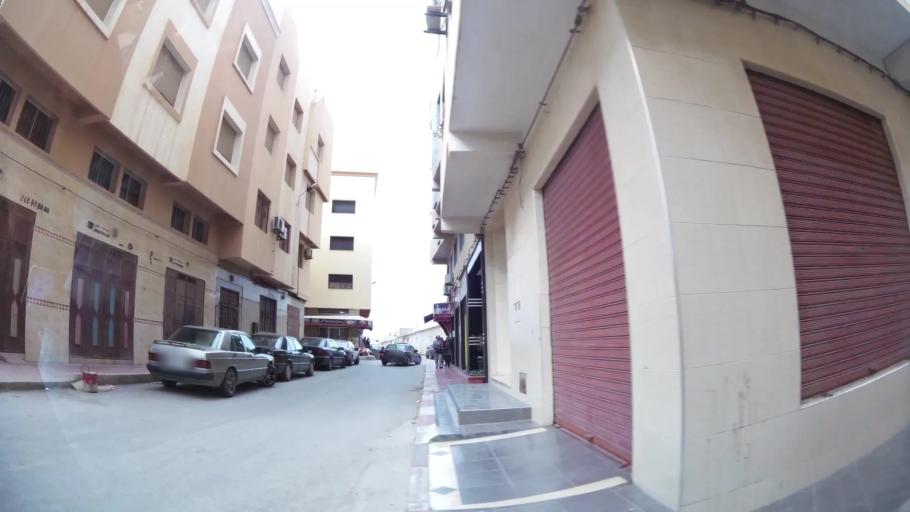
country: MA
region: Oriental
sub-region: Nador
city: Nador
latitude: 35.1703
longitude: -2.9371
